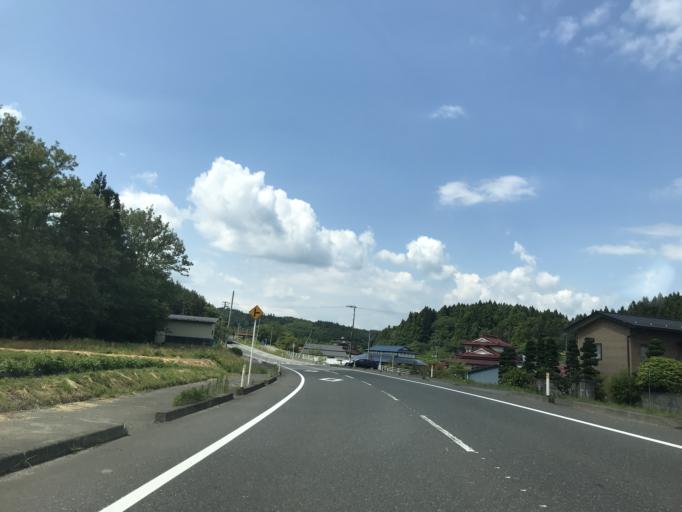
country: JP
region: Miyagi
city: Furukawa
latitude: 38.7287
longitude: 140.9540
